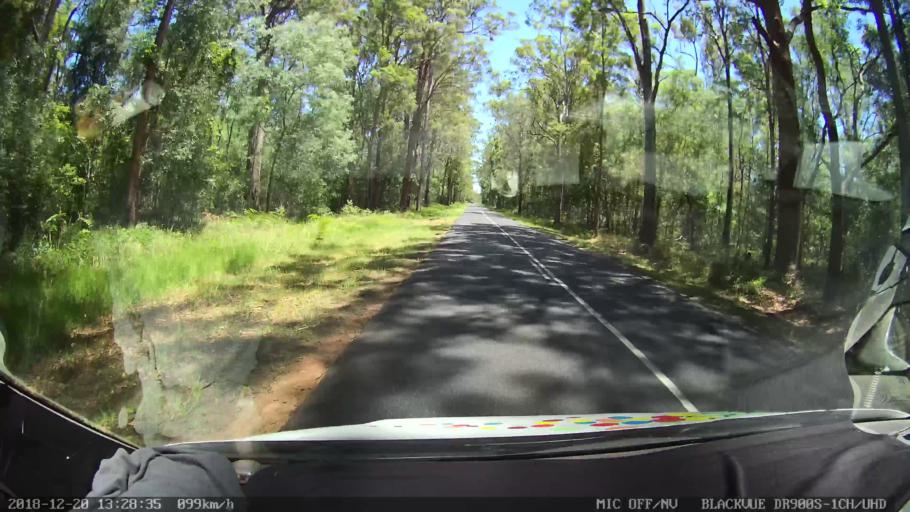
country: AU
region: New South Wales
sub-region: Clarence Valley
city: Gordon
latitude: -29.1768
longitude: 152.9897
